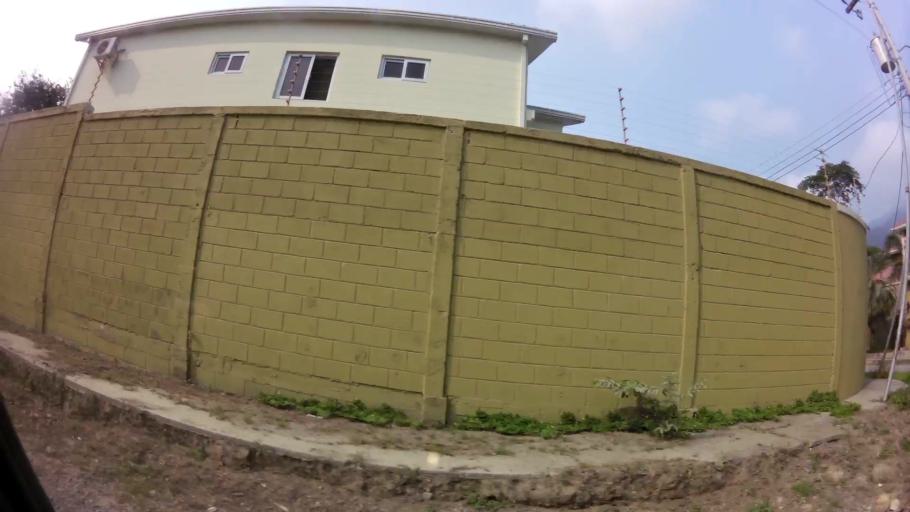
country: HN
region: Cortes
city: El Zapotal del Norte
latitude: 15.5192
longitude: -88.0435
